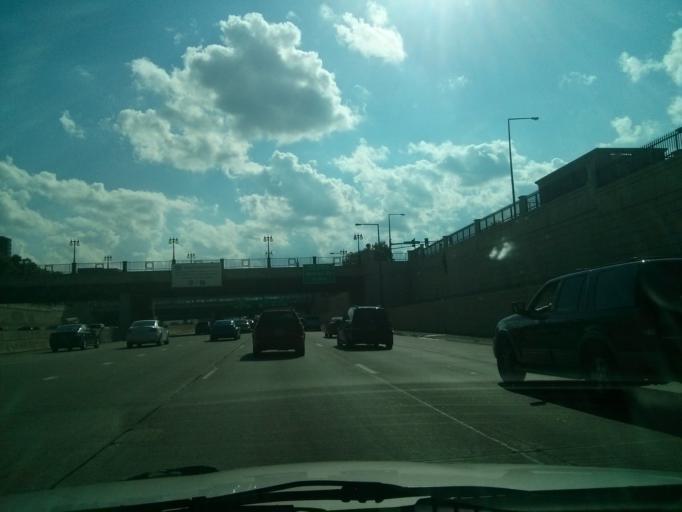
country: US
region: Minnesota
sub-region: Ramsey County
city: Saint Paul
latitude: 44.9526
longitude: -93.0964
